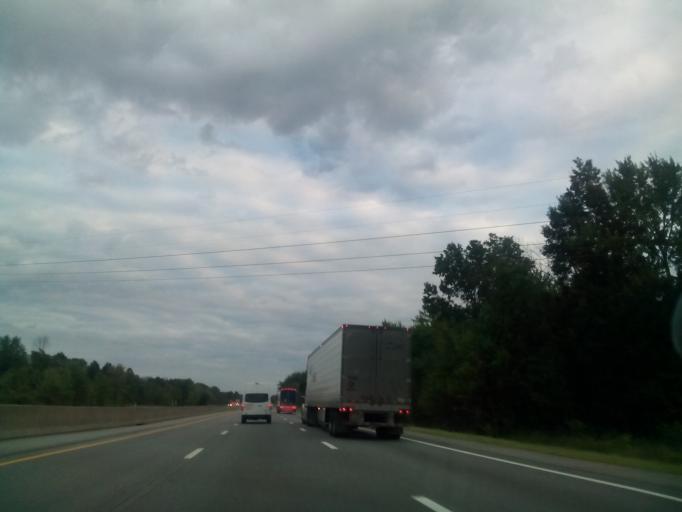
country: US
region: Ohio
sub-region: Trumbull County
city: Lordstown
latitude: 41.1742
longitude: -80.9182
